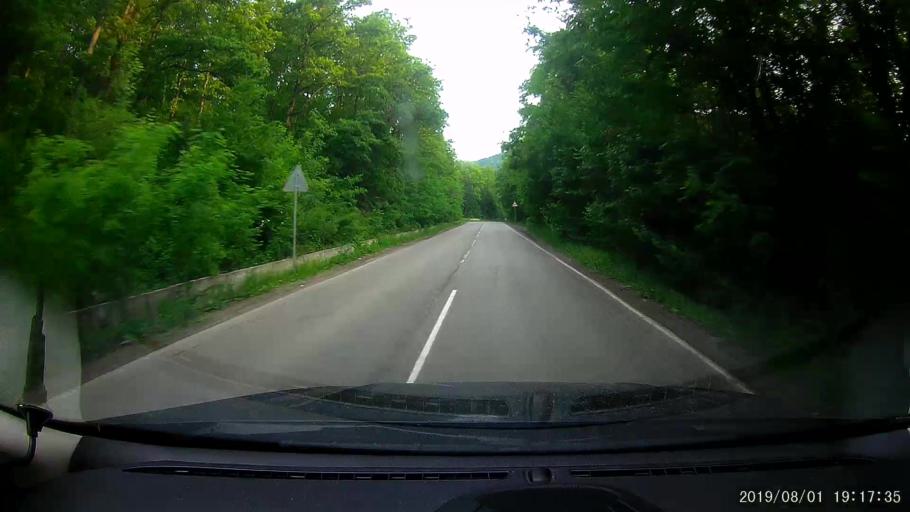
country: BG
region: Shumen
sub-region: Obshtina Smyadovo
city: Smyadovo
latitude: 42.9216
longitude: 26.9410
